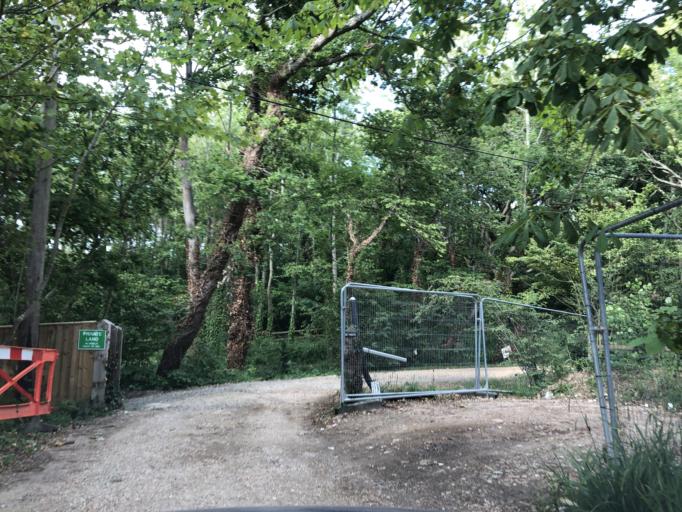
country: GB
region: England
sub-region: Isle of Wight
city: Yarmouth
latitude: 50.7083
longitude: -1.4745
